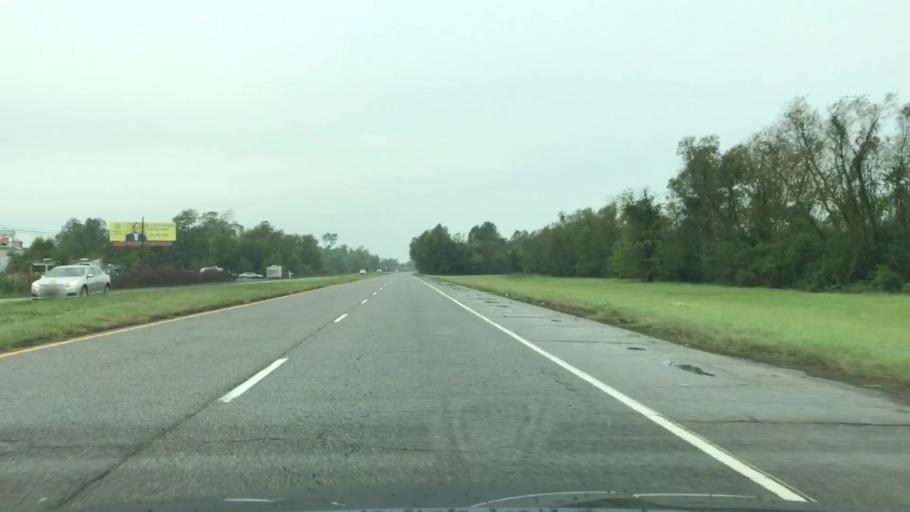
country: US
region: Louisiana
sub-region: Saint Charles Parish
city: Des Allemands
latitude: 29.8024
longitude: -90.5012
